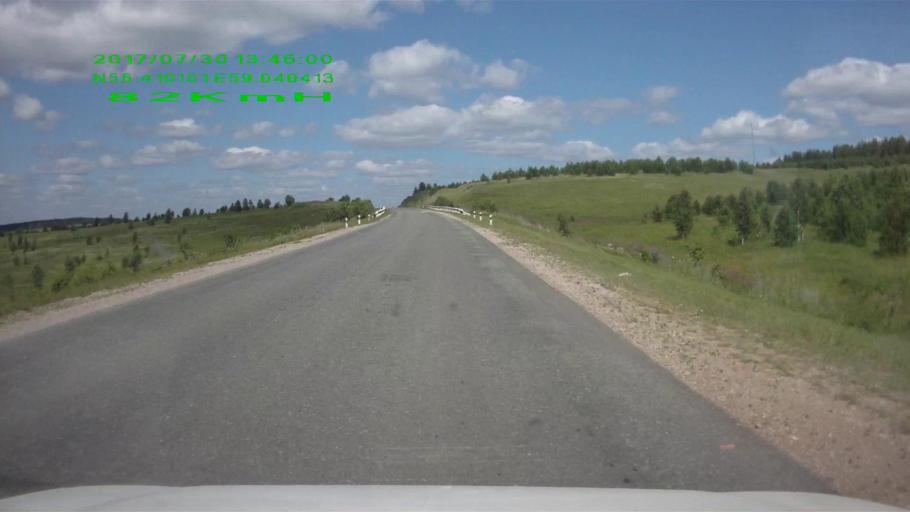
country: RU
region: Sverdlovsk
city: Mikhaylovsk
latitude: 56.4104
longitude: 59.0405
